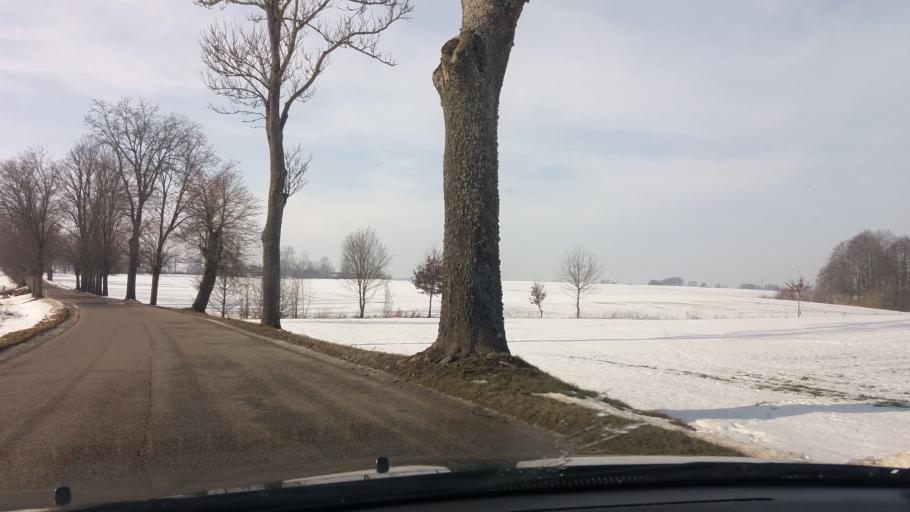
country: PL
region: Warmian-Masurian Voivodeship
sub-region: Powiat olsztynski
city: Jeziorany
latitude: 54.1030
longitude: 20.7323
